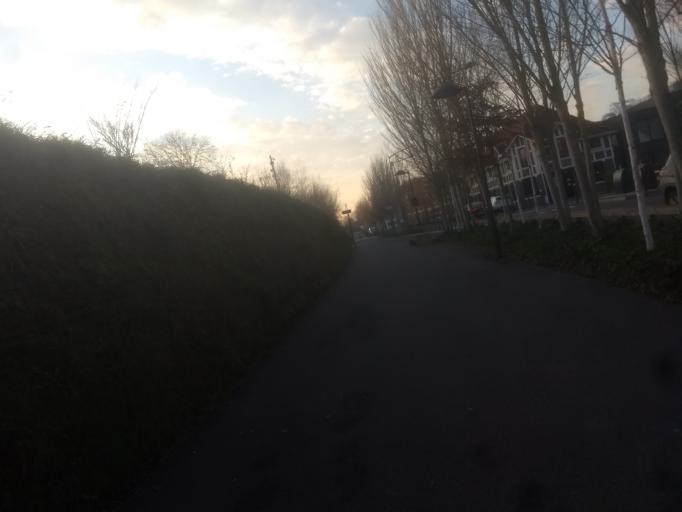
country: FR
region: Nord-Pas-de-Calais
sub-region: Departement du Pas-de-Calais
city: Eleu-dit-Leauwette
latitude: 50.4316
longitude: 2.8083
